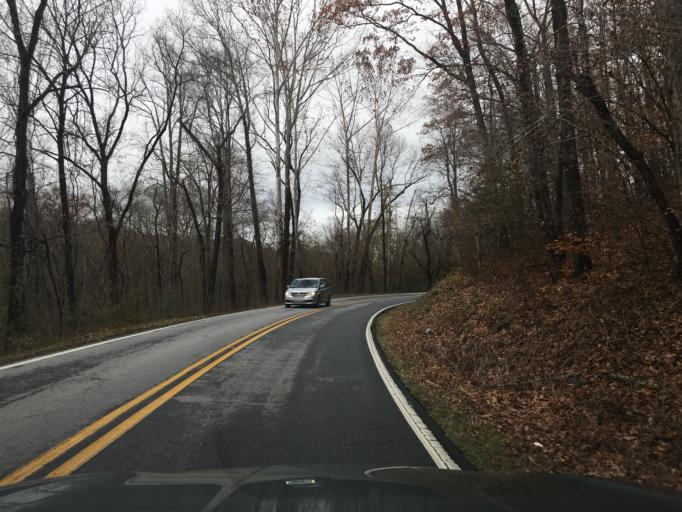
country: US
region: North Carolina
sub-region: Rutherford County
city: Rutherfordton
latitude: 35.3077
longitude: -81.9852
